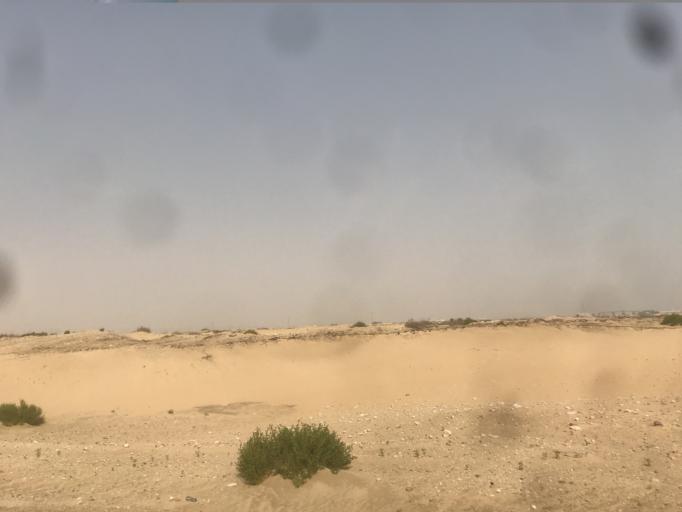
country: SA
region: Eastern Province
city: Abqaiq
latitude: 25.9093
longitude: 49.9348
